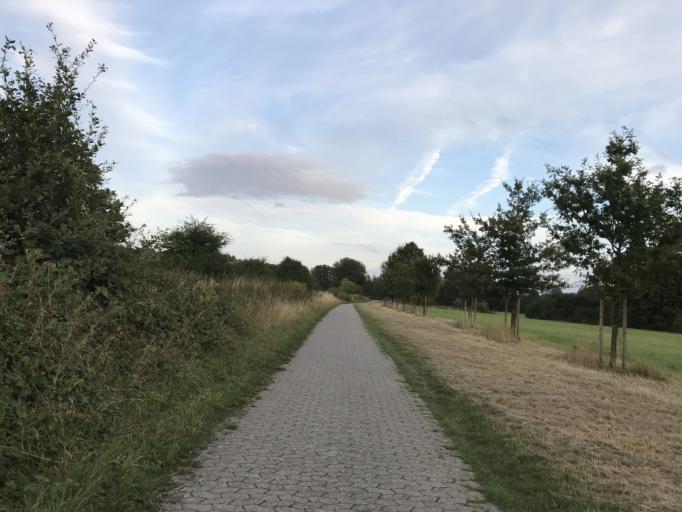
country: DE
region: North Rhine-Westphalia
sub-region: Regierungsbezirk Detmold
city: Lemgo
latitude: 52.0229
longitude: 8.9395
